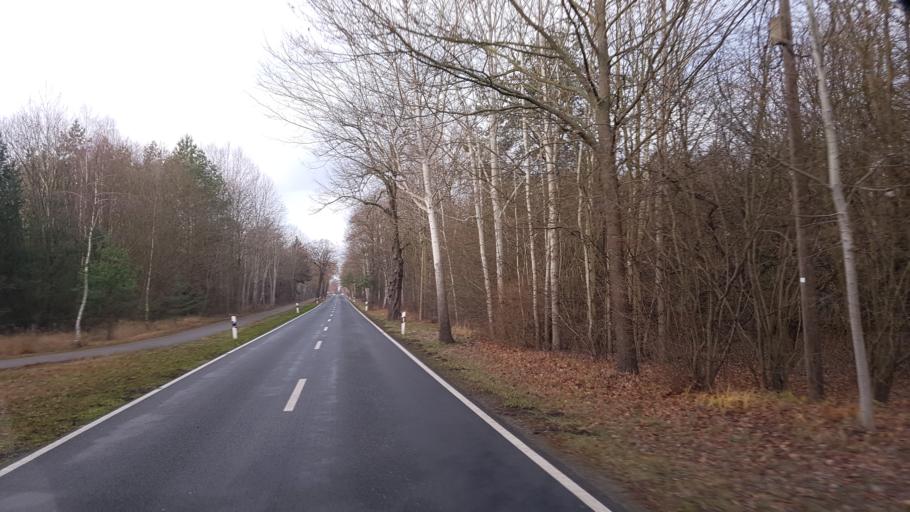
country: DE
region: Brandenburg
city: Sallgast
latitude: 51.5935
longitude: 13.8033
